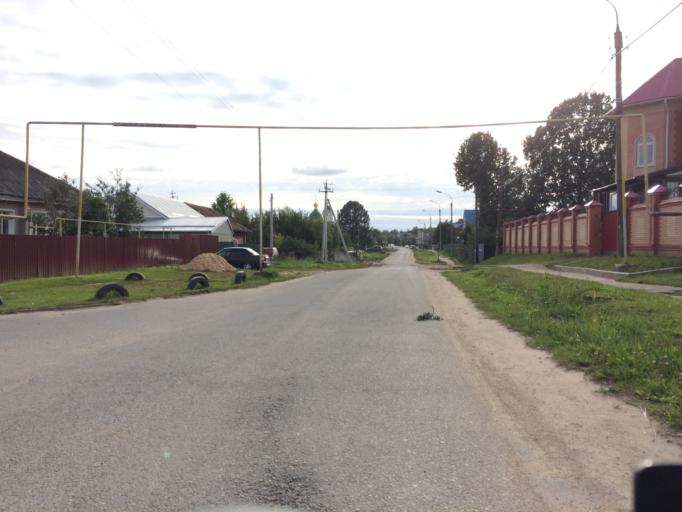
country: RU
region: Mariy-El
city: Yoshkar-Ola
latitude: 56.6520
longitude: 47.9851
